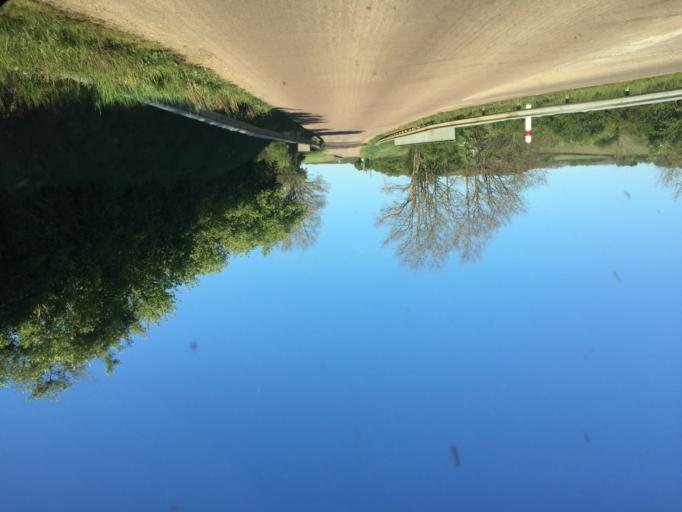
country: FR
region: Bourgogne
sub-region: Departement de la Nievre
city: Clamecy
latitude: 47.4853
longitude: 3.5170
